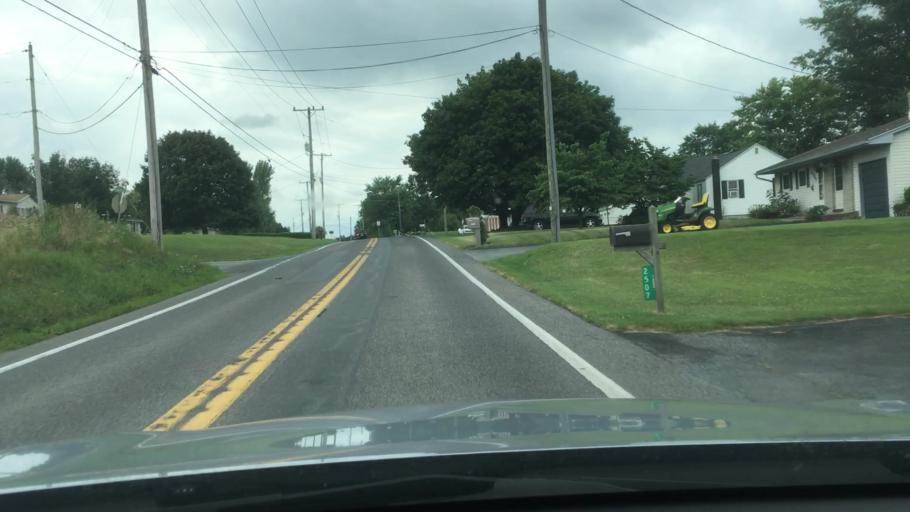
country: US
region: Pennsylvania
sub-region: Franklin County
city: Greencastle
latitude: 39.8773
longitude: -77.7286
